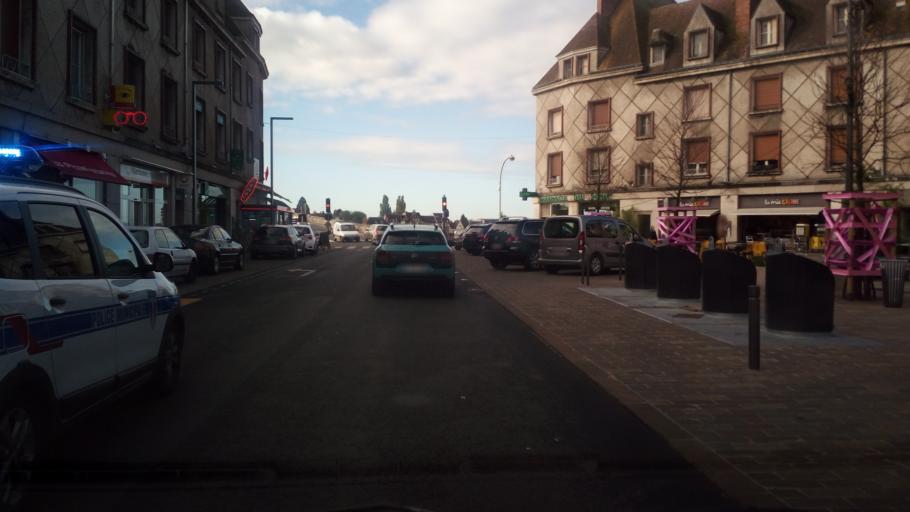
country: FR
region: Centre
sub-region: Departement du Loiret
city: Gien
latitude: 47.6843
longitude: 2.6323
